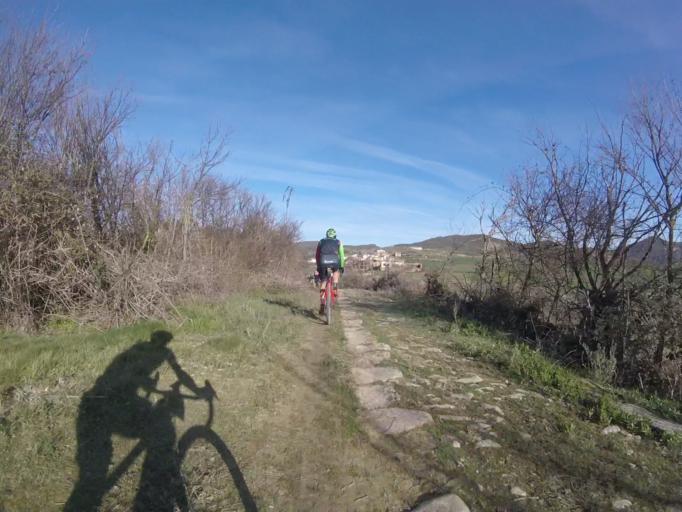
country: ES
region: Navarre
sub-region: Provincia de Navarra
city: Yerri
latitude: 42.6888
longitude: -1.9573
